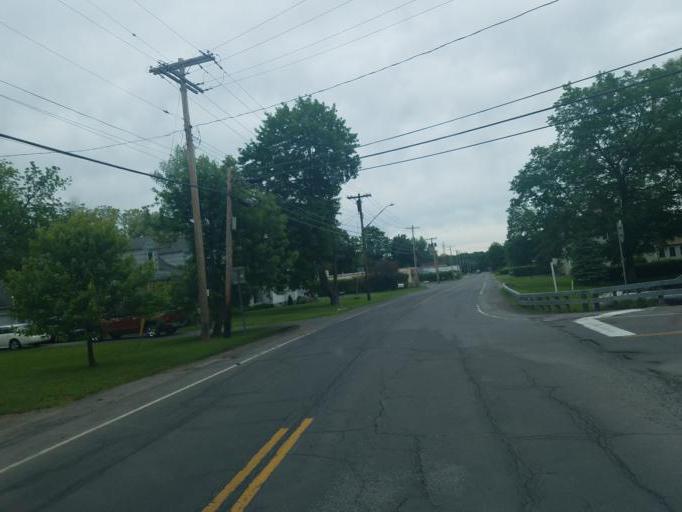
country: US
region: New York
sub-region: Herkimer County
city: Ilion
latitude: 42.9978
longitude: -75.0512
